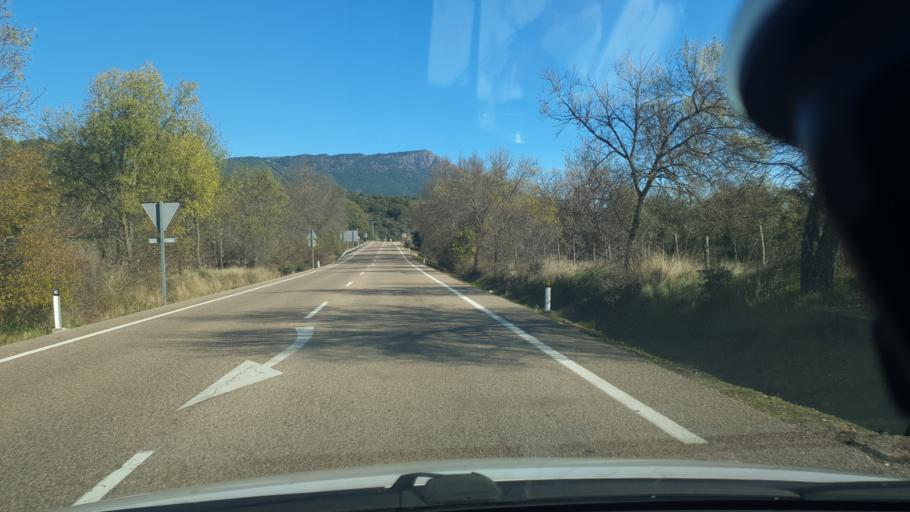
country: ES
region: Castille and Leon
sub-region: Provincia de Avila
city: Arenas de San Pedro
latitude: 40.1810
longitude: -5.0384
